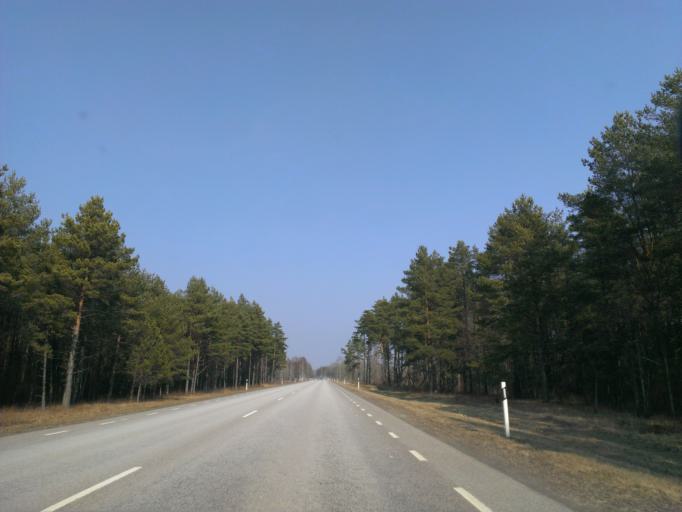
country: EE
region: Saare
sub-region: Orissaare vald
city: Orissaare
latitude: 58.4496
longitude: 22.8005
